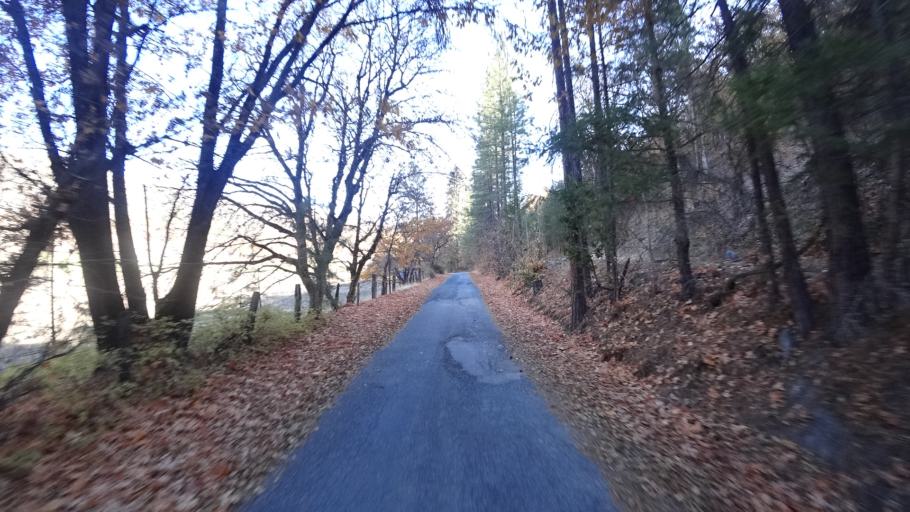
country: US
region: California
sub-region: Siskiyou County
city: Yreka
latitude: 41.8373
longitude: -122.9332
